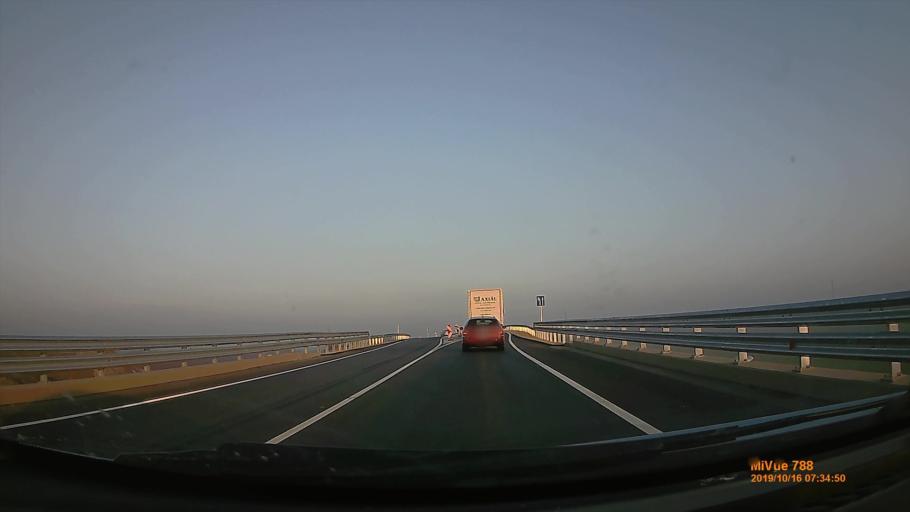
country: HU
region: Heves
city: Kerecsend
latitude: 47.7753
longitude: 20.3750
